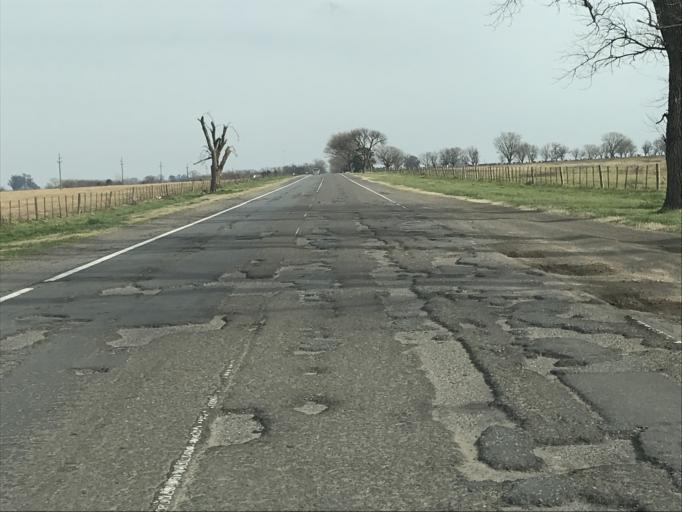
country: AR
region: Santa Fe
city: Armstrong
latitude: -32.7583
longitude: -61.6962
